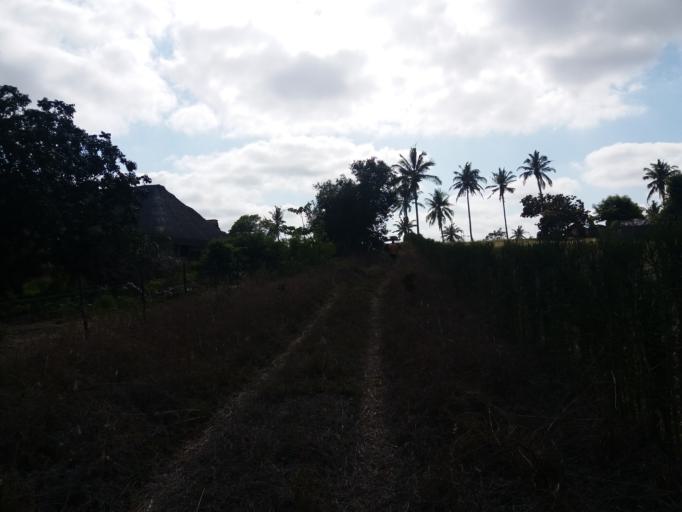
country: MZ
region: Inhambane
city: Inhambane
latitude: -23.9247
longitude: 35.3906
